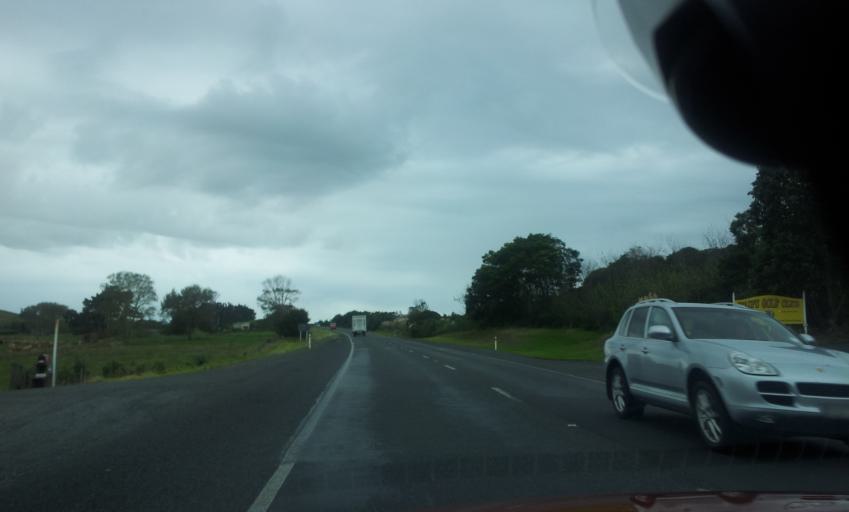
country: NZ
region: Northland
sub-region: Whangarei
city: Ruakaka
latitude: -35.9434
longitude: 174.4557
